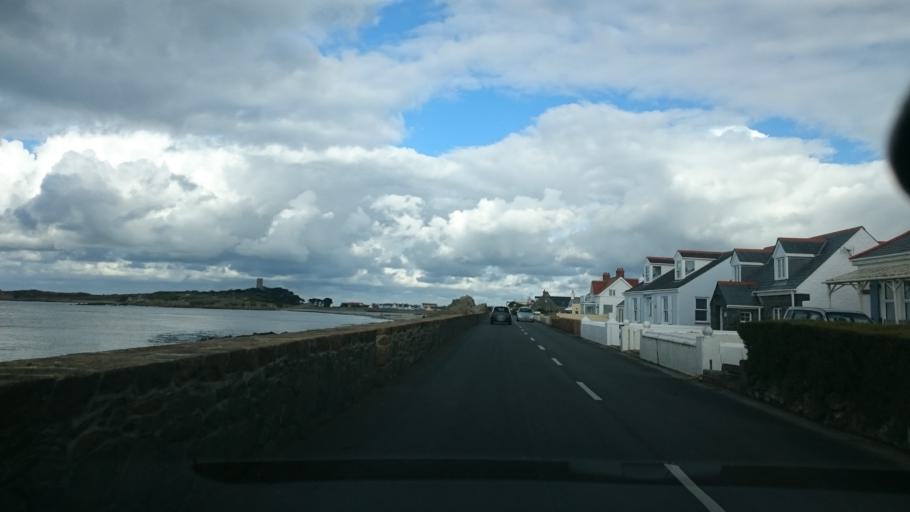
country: GG
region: St Peter Port
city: Saint Peter Port
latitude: 49.4491
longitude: -2.6496
